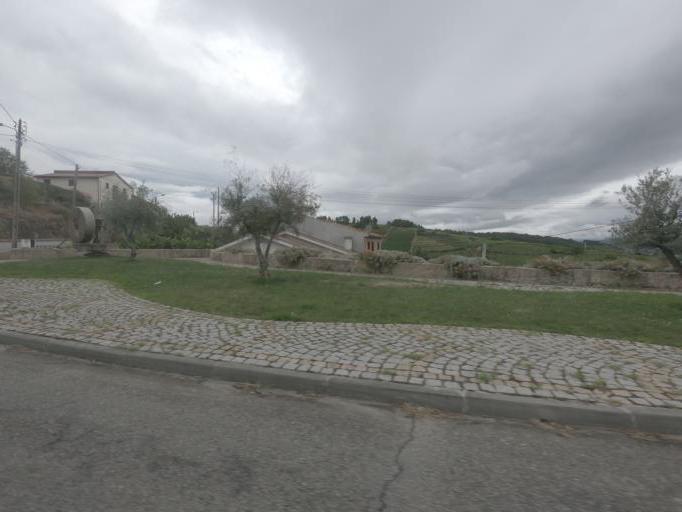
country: PT
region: Vila Real
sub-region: Sabrosa
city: Sabrosa
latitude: 41.2885
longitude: -7.5163
